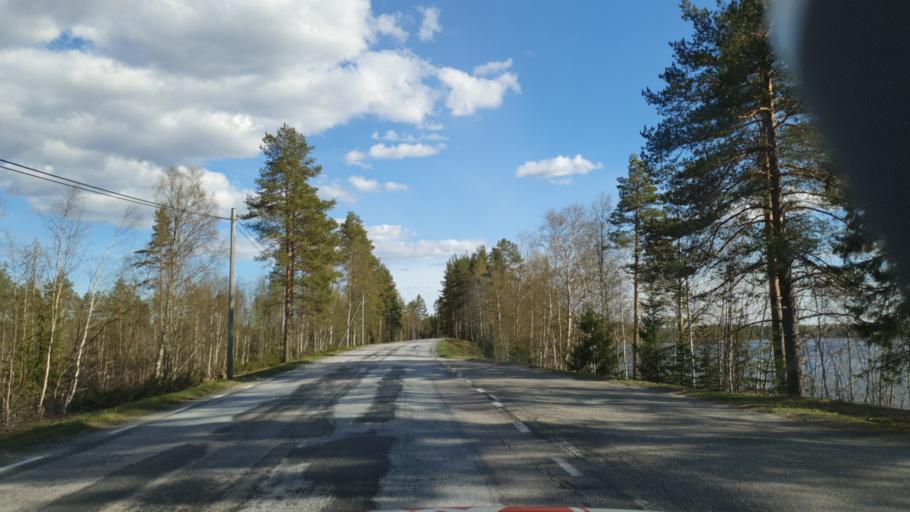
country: SE
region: Vaesterbotten
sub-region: Umea Kommun
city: Roback
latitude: 63.9088
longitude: 20.1499
